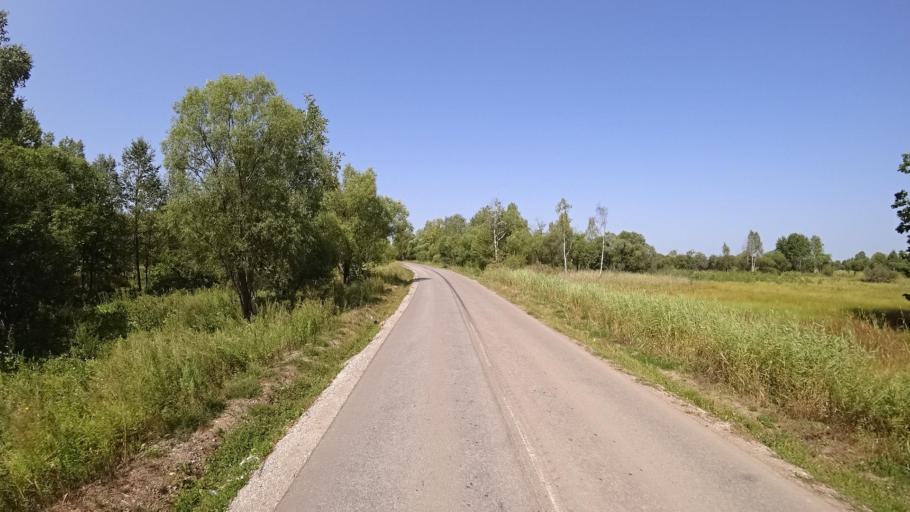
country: RU
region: Khabarovsk Krai
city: Khor
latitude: 47.9756
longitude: 135.1127
